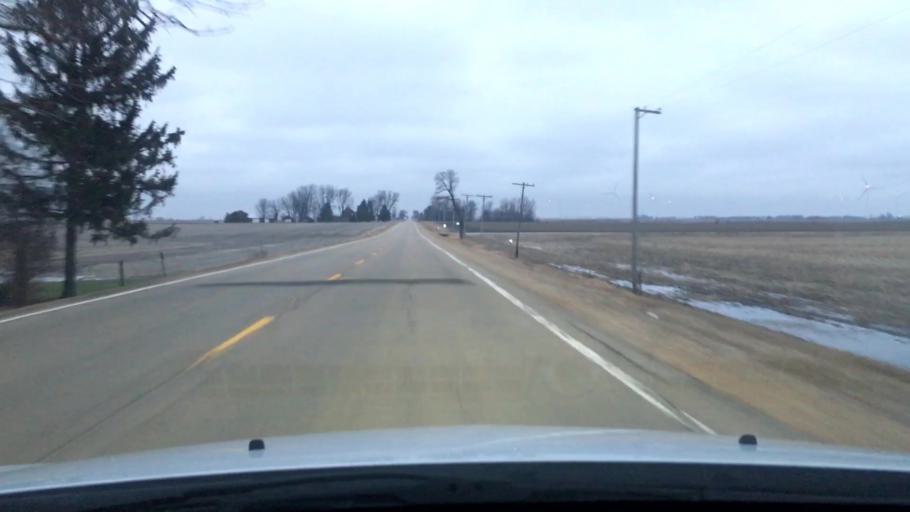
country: US
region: Illinois
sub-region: LaSalle County
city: Mendota
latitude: 41.6404
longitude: -89.1294
